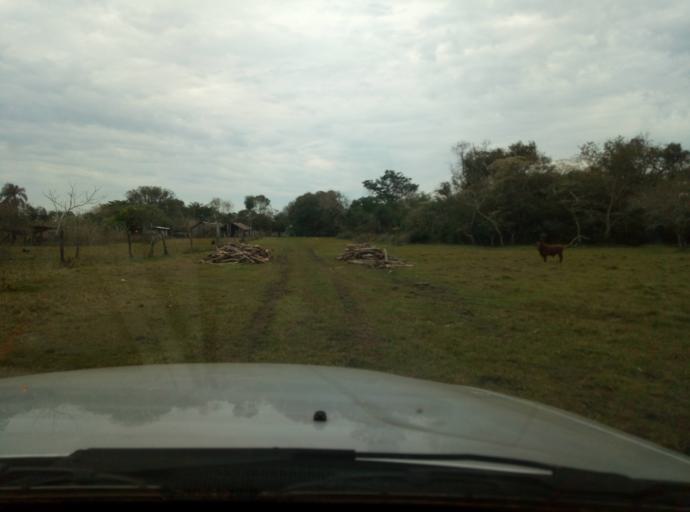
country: PY
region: Caaguazu
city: Carayao
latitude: -25.1637
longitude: -56.3330
